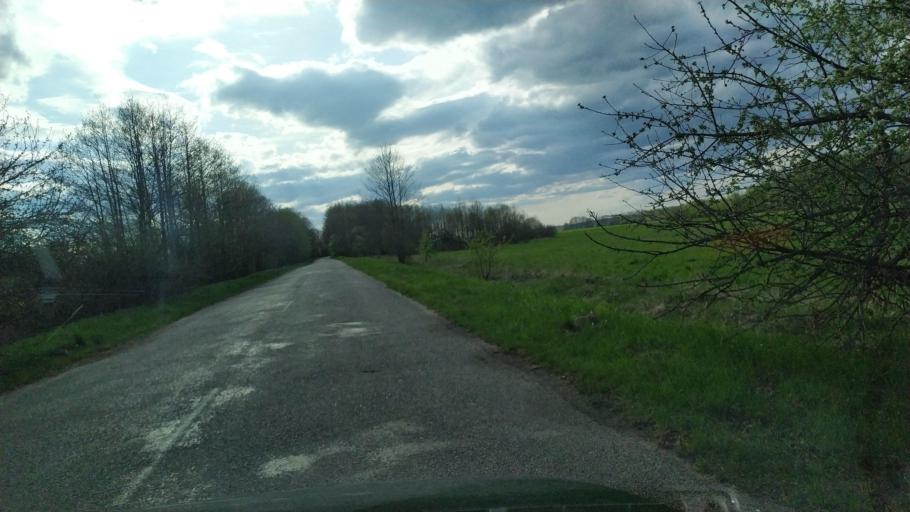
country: BY
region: Brest
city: Pruzhany
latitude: 52.7011
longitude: 24.1977
